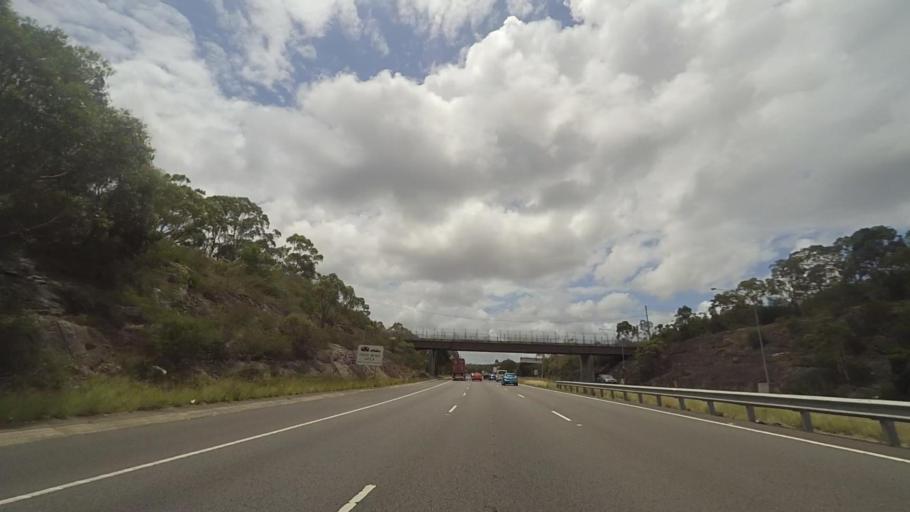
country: AU
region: New South Wales
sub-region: Gosford Shire
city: Point Clare
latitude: -33.4458
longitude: 151.2185
